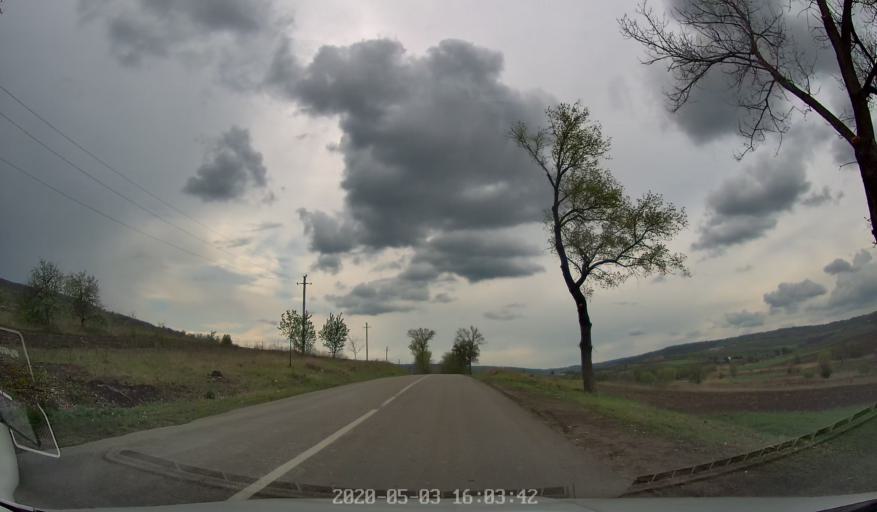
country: MD
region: Stinga Nistrului
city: Bucovat
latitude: 47.1818
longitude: 28.3775
